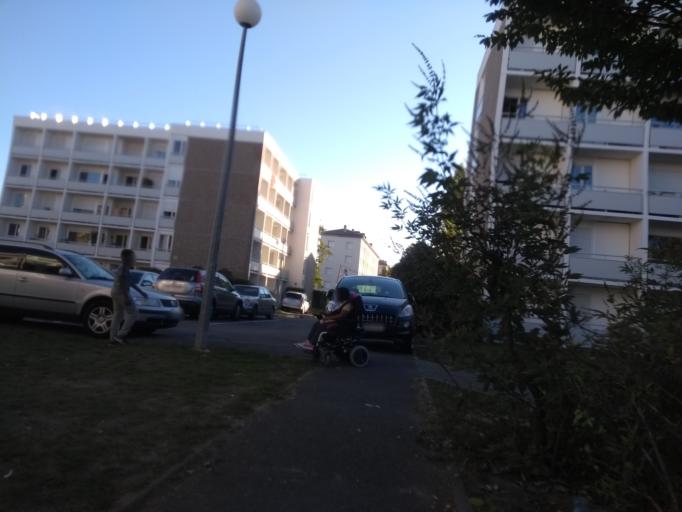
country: FR
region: Aquitaine
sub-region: Departement de la Gironde
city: Talence
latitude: 44.8056
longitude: -0.5887
